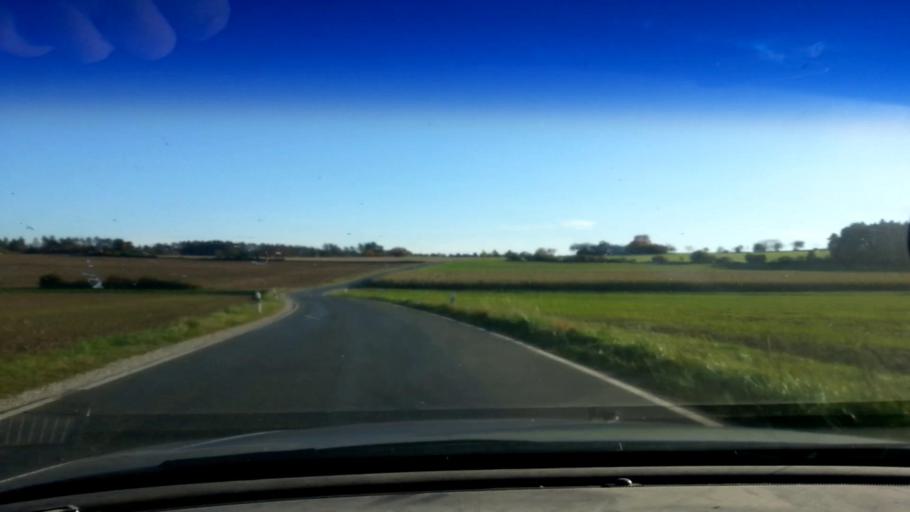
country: DE
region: Bavaria
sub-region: Upper Franconia
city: Poxdorf
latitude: 49.9002
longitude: 11.0923
